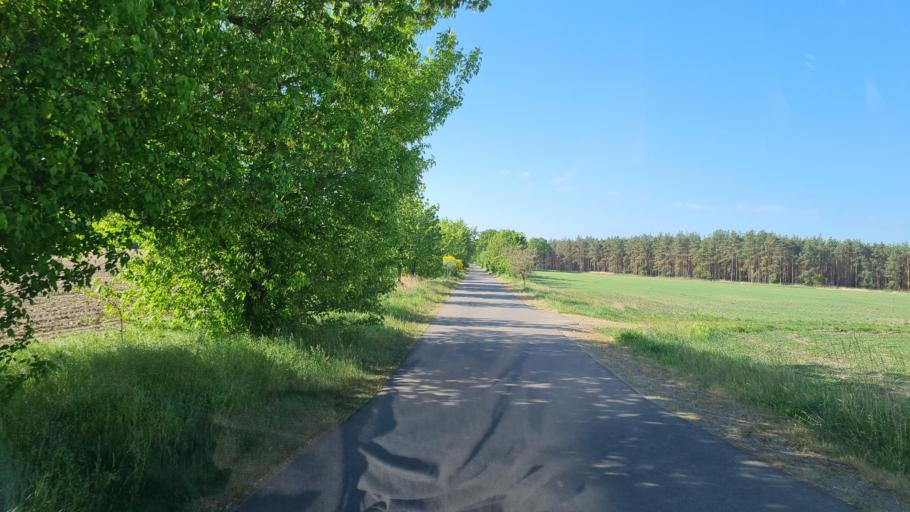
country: DE
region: Brandenburg
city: Falkenberg
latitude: 51.6134
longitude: 13.2054
